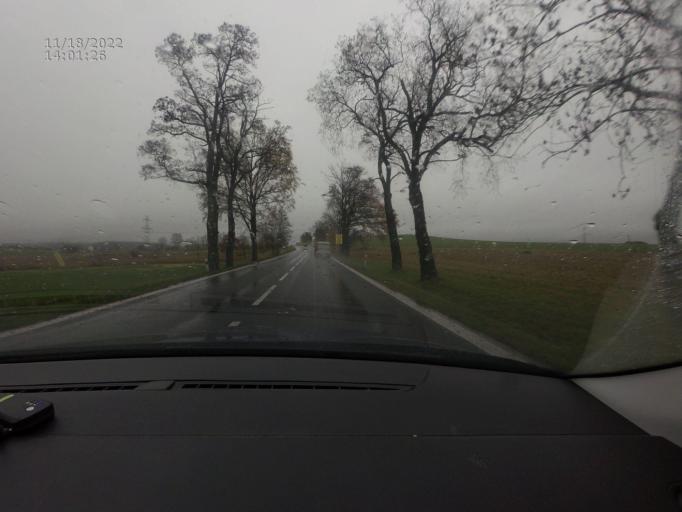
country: CZ
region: Jihocesky
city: Mirotice
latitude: 49.3502
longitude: 14.0403
